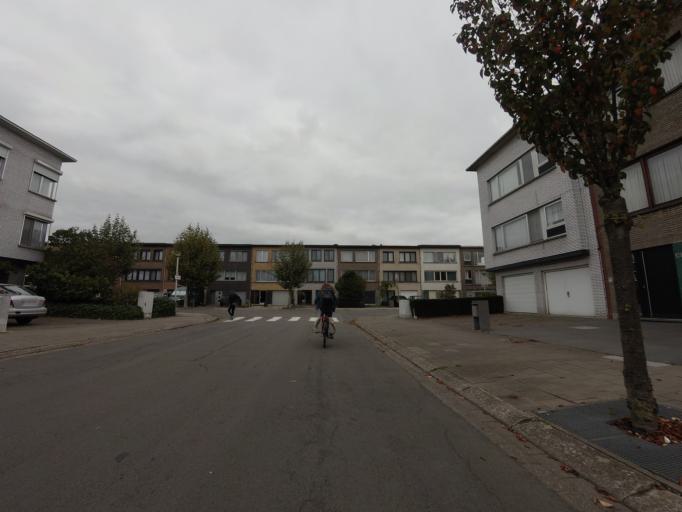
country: BE
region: Flanders
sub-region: Provincie Antwerpen
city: Antwerpen
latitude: 51.2588
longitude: 4.4349
